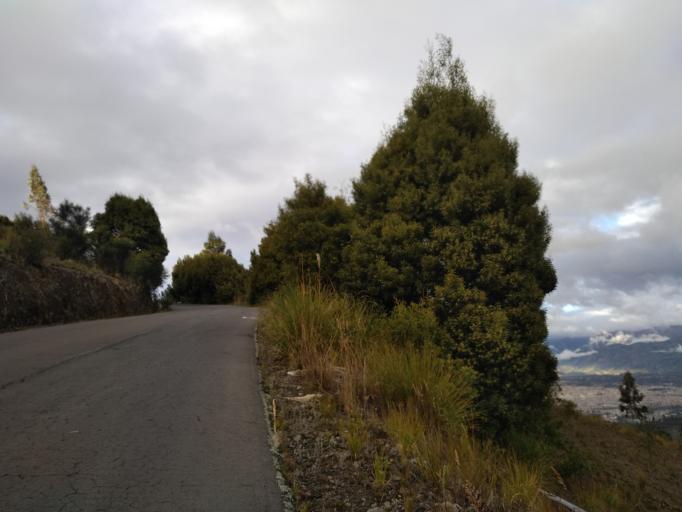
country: EC
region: Chimborazo
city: Riobamba
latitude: -1.7002
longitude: -78.7092
